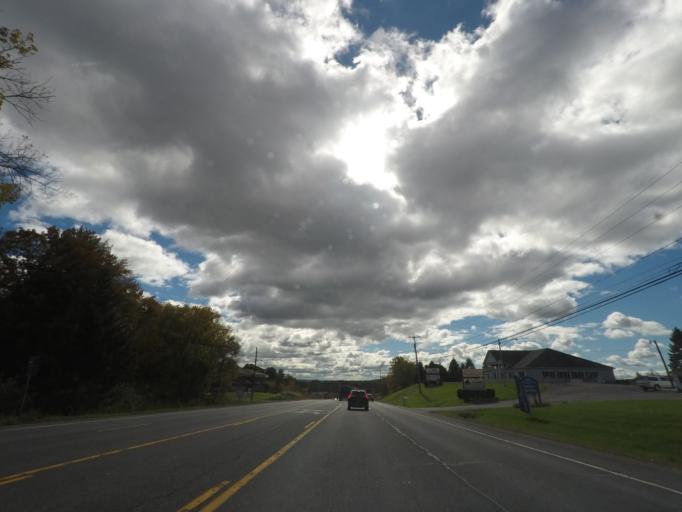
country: US
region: New York
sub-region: Albany County
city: Cohoes
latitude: 42.8264
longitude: -73.7343
